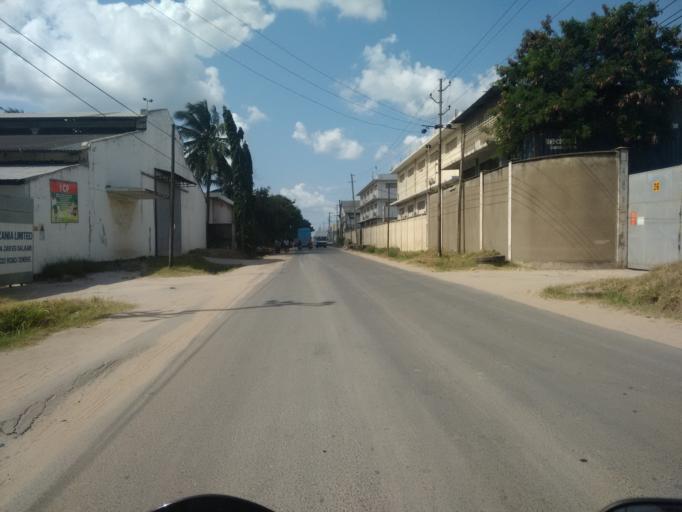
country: TZ
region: Dar es Salaam
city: Dar es Salaam
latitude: -6.8406
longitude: 39.2640
